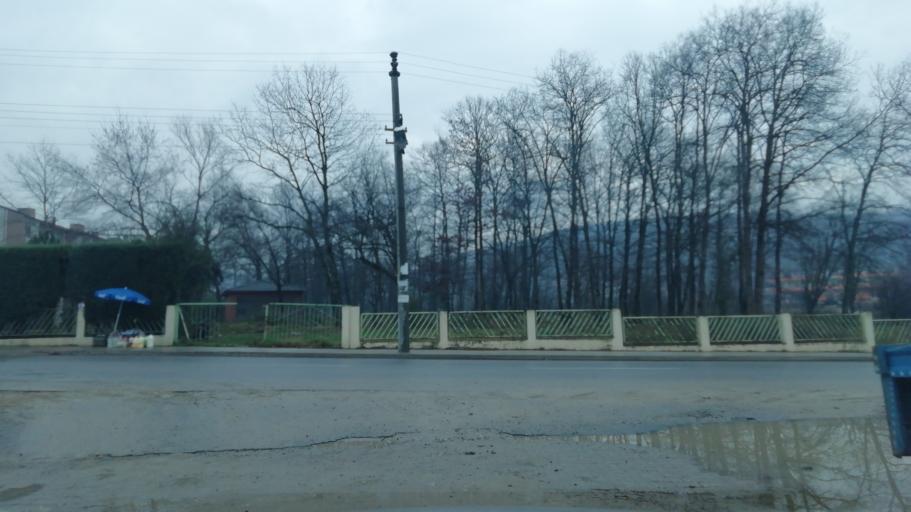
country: TR
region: Sakarya
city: Akyazi
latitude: 40.6252
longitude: 30.6526
